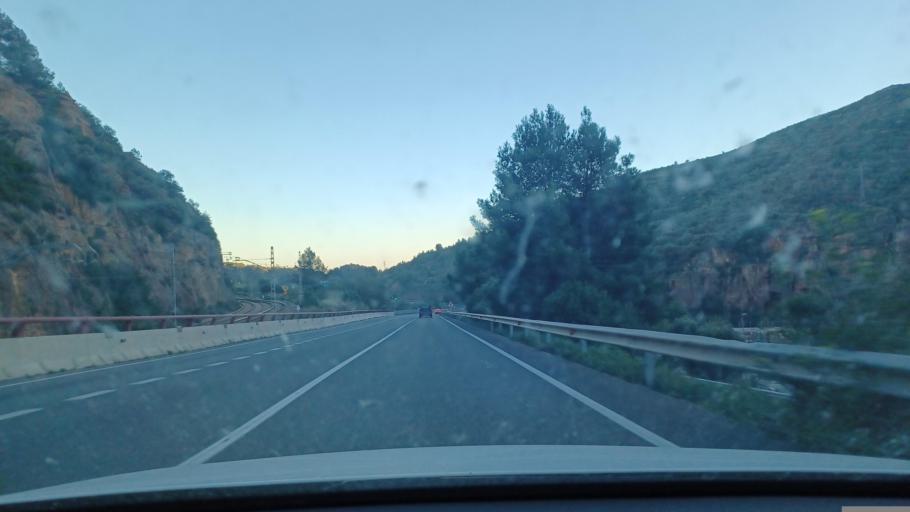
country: ES
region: Catalonia
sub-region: Provincia de Tarragona
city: Alcover
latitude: 41.3089
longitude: 1.1911
